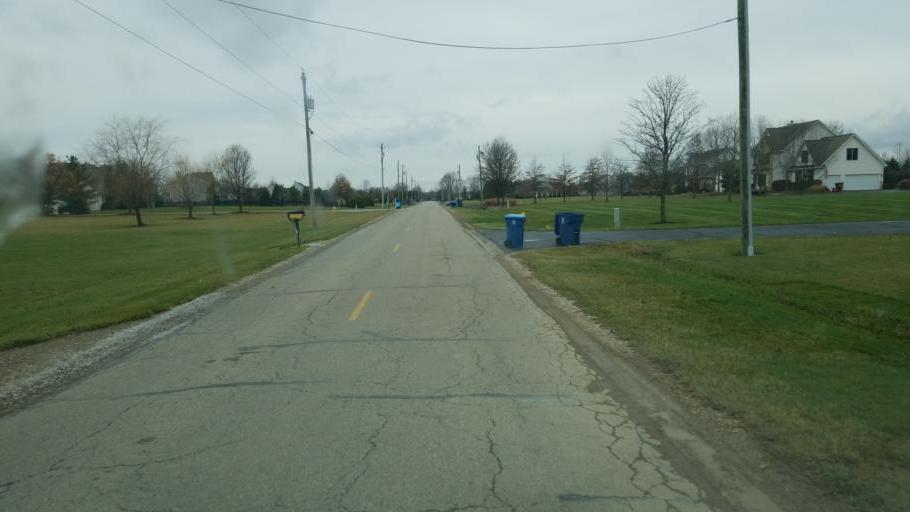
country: US
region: Ohio
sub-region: Delaware County
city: Powell
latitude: 40.2291
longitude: -83.1218
